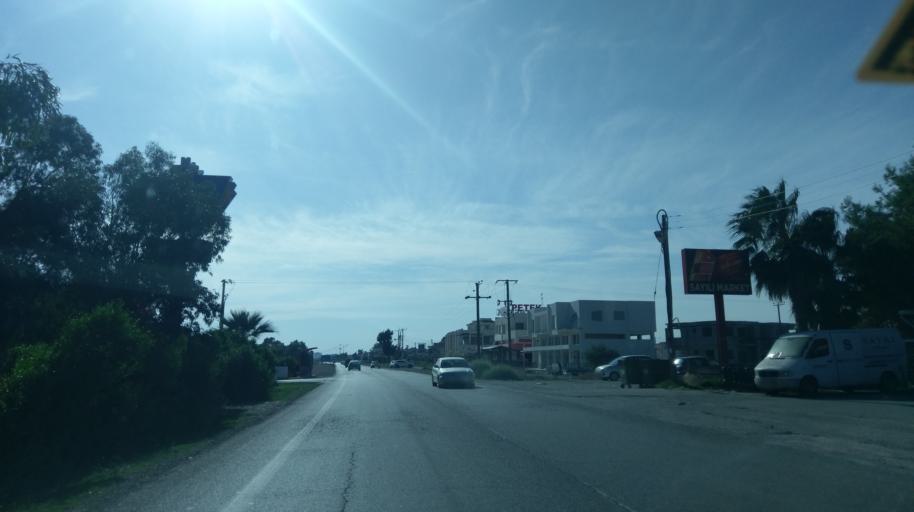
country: CY
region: Ammochostos
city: Trikomo
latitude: 35.2827
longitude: 33.9236
